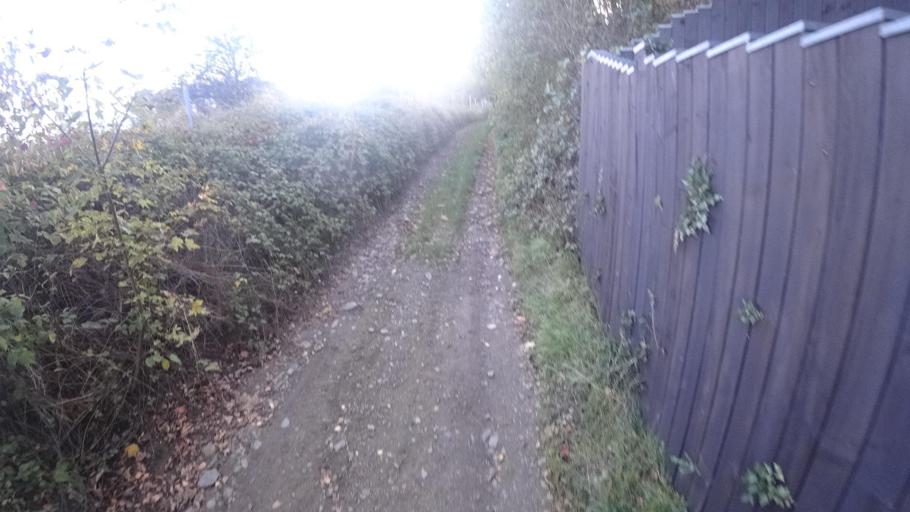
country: DE
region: Rheinland-Pfalz
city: Altenahr
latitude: 50.5066
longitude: 6.9757
